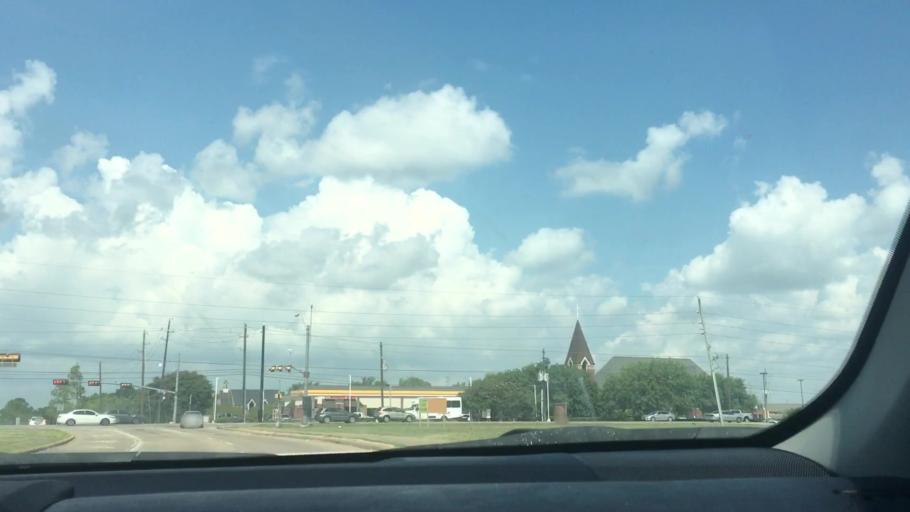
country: US
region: Texas
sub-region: Fort Bend County
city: Fifth Street
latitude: 29.6008
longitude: -95.5634
